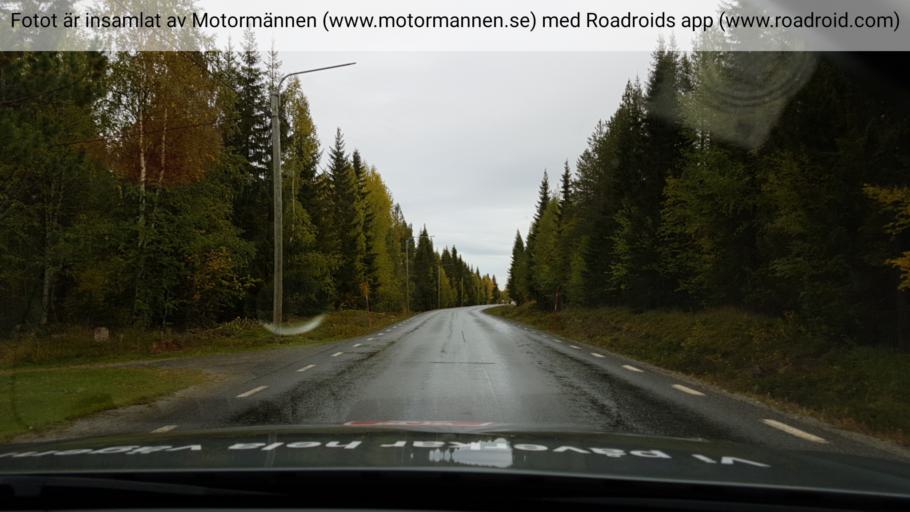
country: SE
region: Vaesterbotten
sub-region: Vilhelmina Kommun
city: Sjoberg
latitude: 64.6522
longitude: 16.3260
